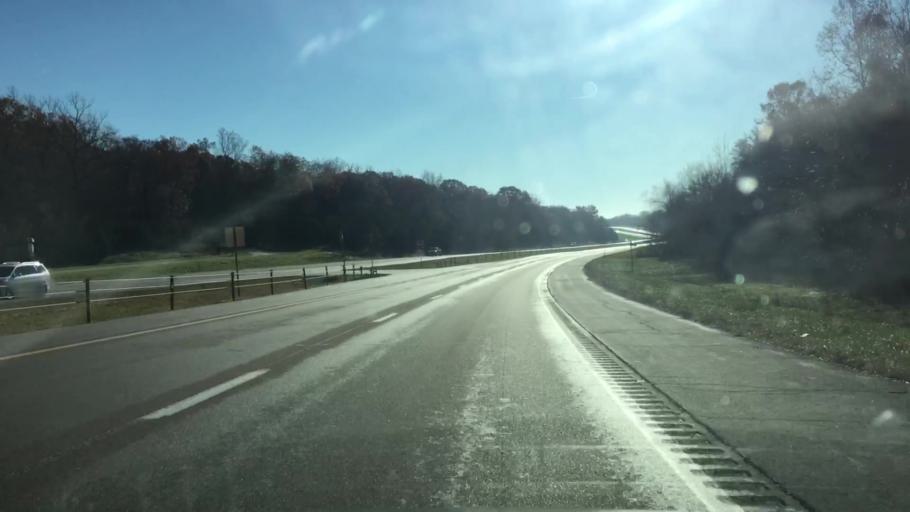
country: US
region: Missouri
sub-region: Cole County
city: Jefferson City
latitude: 38.6678
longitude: -92.2293
